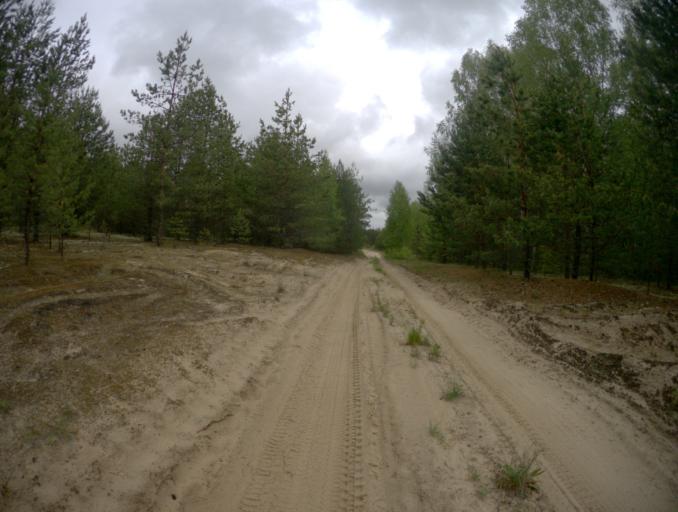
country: RU
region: Rjazan
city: Gus'-Zheleznyy
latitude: 55.1985
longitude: 41.0692
